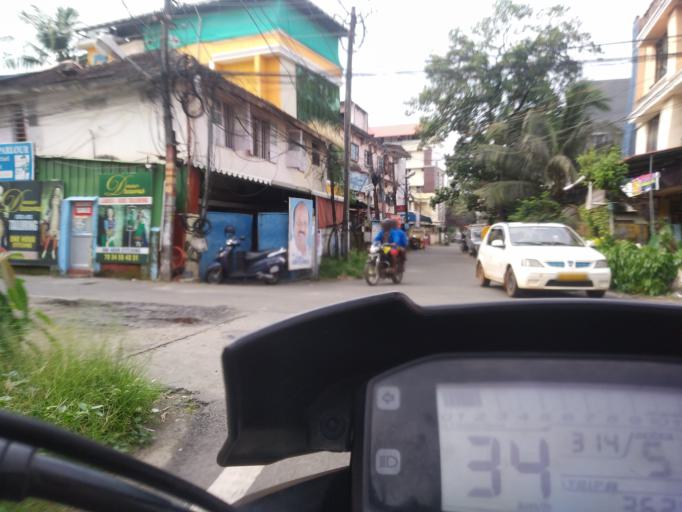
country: IN
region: Kerala
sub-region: Ernakulam
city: Cochin
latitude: 9.9759
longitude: 76.2868
